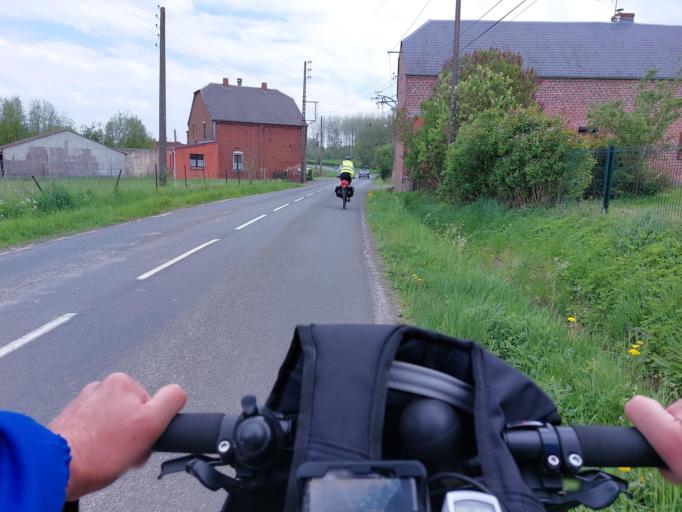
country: FR
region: Nord-Pas-de-Calais
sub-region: Departement du Nord
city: La Longueville
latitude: 50.2724
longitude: 3.8870
